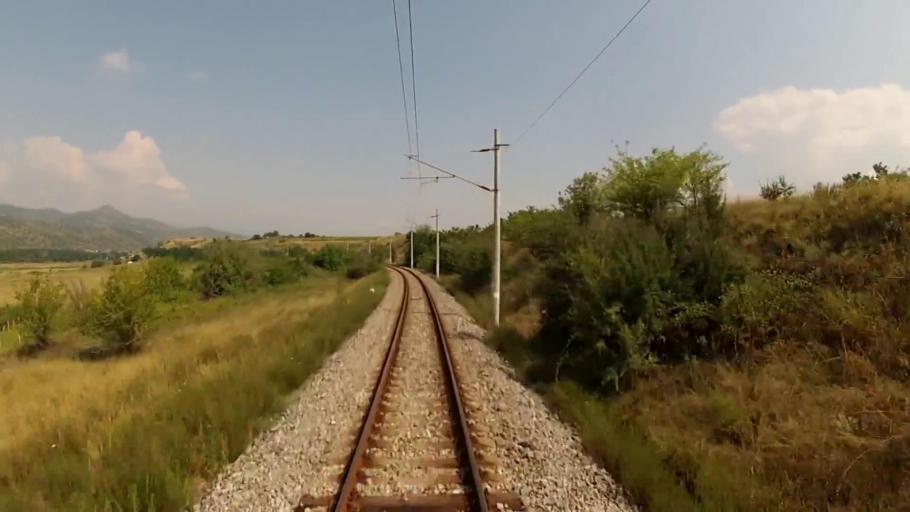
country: BG
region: Blagoevgrad
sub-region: Obshtina Sandanski
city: Sandanski
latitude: 41.5622
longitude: 23.2416
